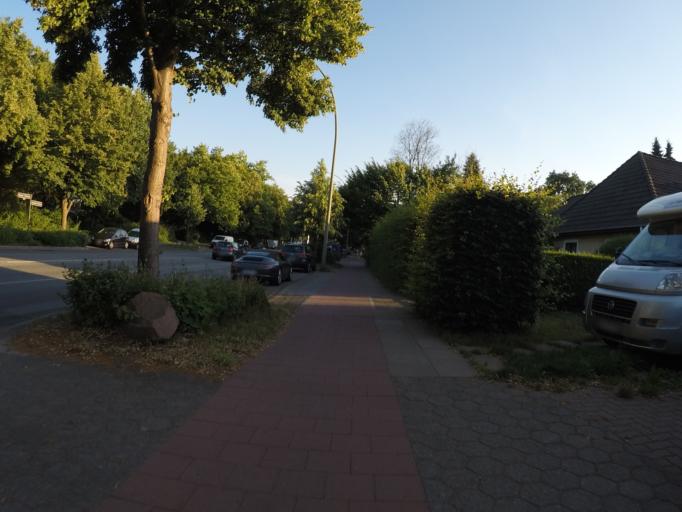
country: DE
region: Hamburg
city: Wellingsbuettel
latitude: 53.6337
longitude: 10.0903
